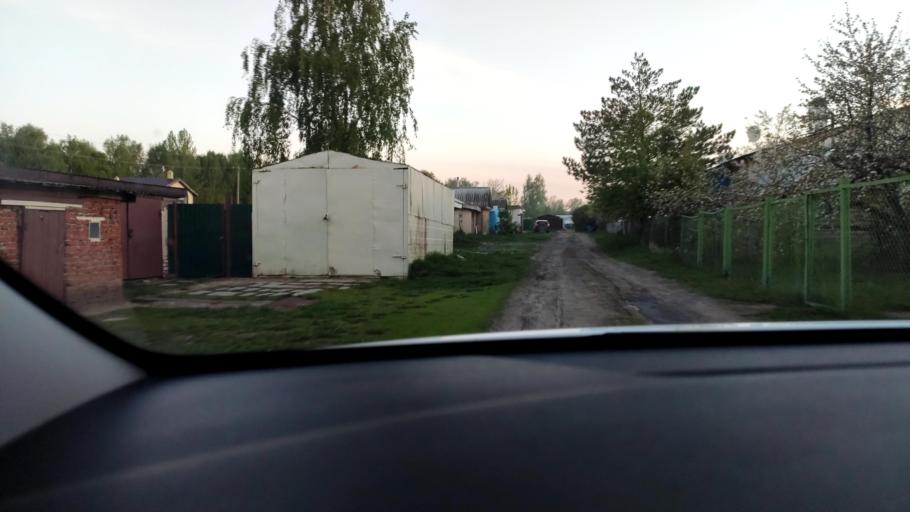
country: RU
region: Tatarstan
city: Stolbishchi
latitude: 55.7385
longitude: 49.2723
